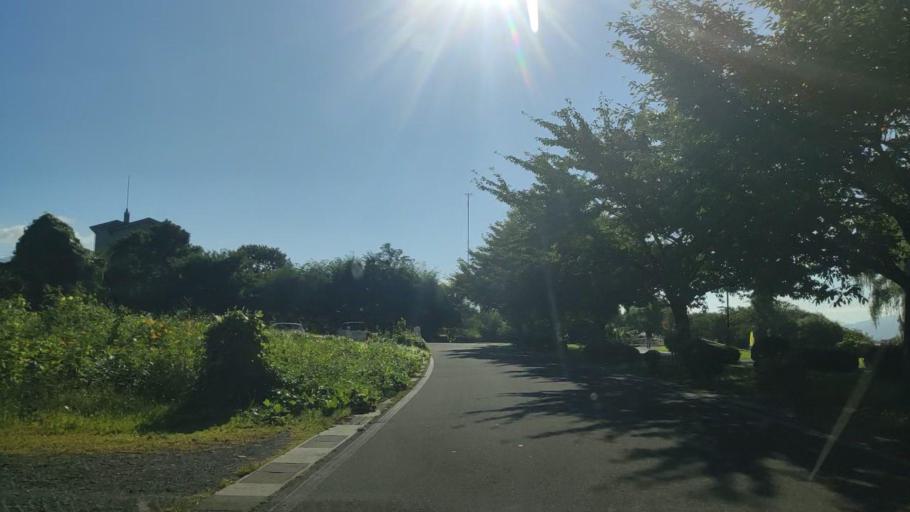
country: JP
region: Nagano
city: Okaya
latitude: 36.0584
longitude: 138.0644
